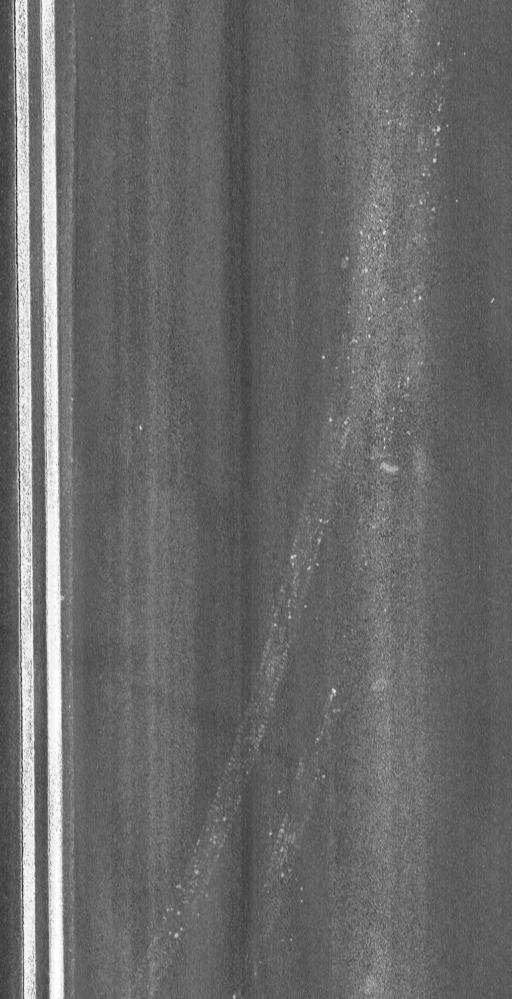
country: US
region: Vermont
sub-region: Chittenden County
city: Burlington
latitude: 44.3755
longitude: -73.2259
